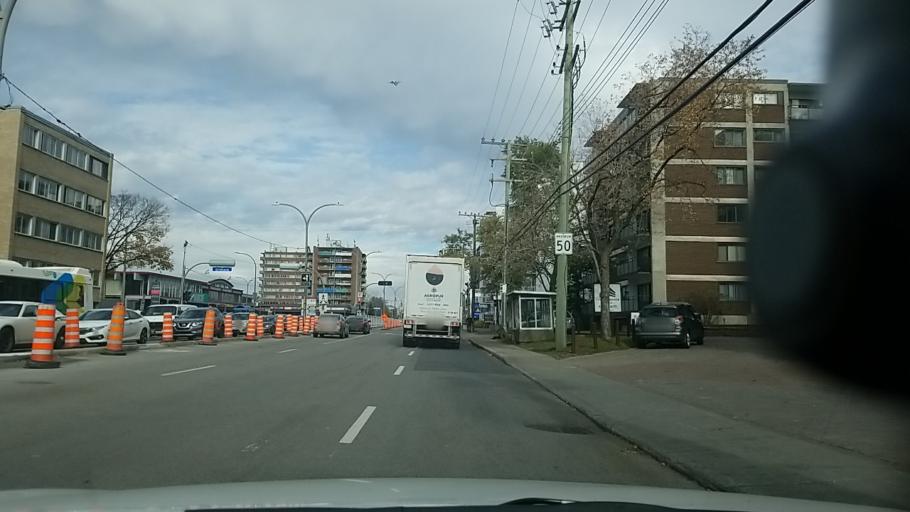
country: CA
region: Quebec
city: Mont-Royal
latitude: 45.5269
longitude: -73.6701
